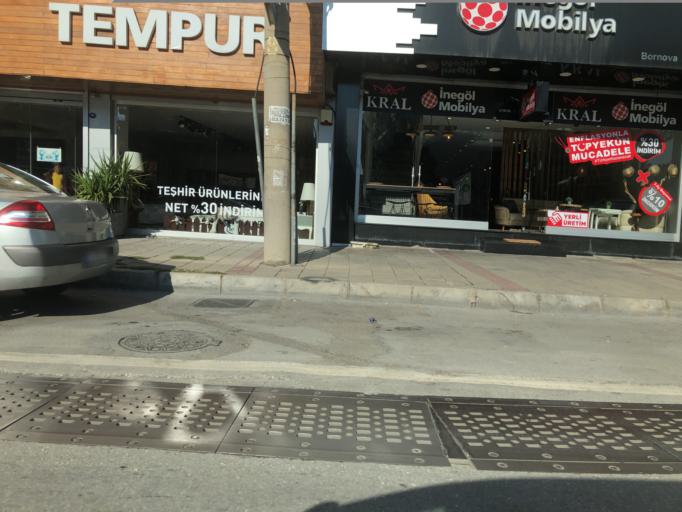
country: TR
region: Izmir
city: Bornova
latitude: 38.4570
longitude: 27.1853
